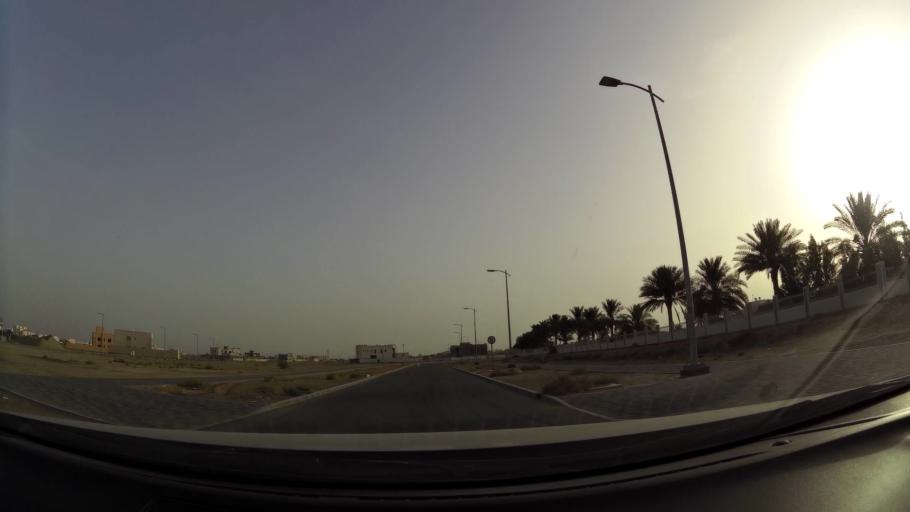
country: AE
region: Abu Dhabi
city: Al Ain
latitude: 24.1042
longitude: 55.7153
